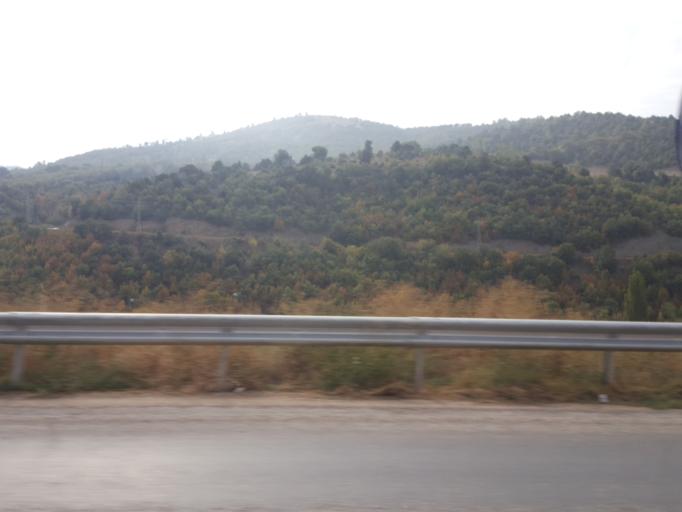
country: TR
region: Amasya
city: Gediksaray
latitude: 40.4899
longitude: 35.7879
